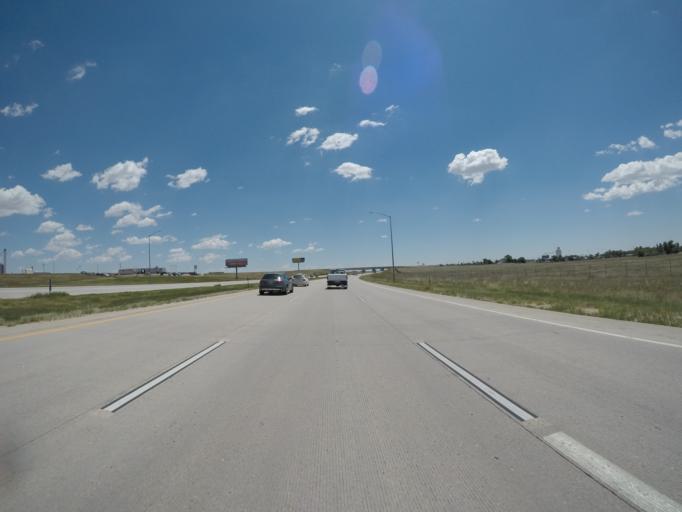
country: US
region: Colorado
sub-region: Lincoln County
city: Limon
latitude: 39.2723
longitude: -103.6817
